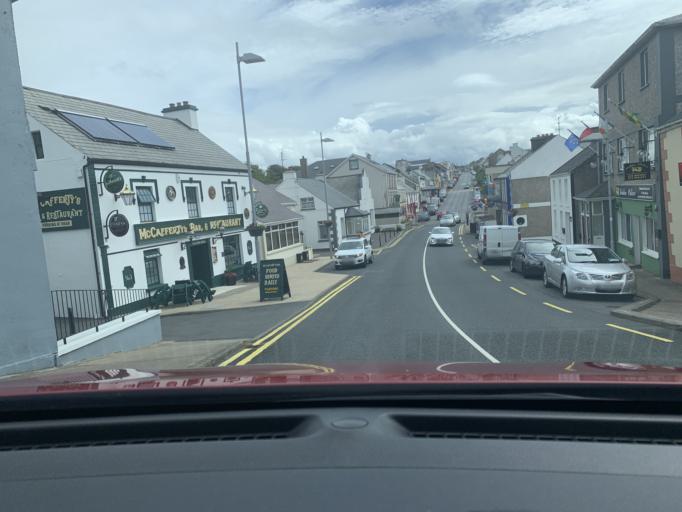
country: IE
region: Ulster
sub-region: County Donegal
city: Dungloe
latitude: 54.9514
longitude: -8.3613
